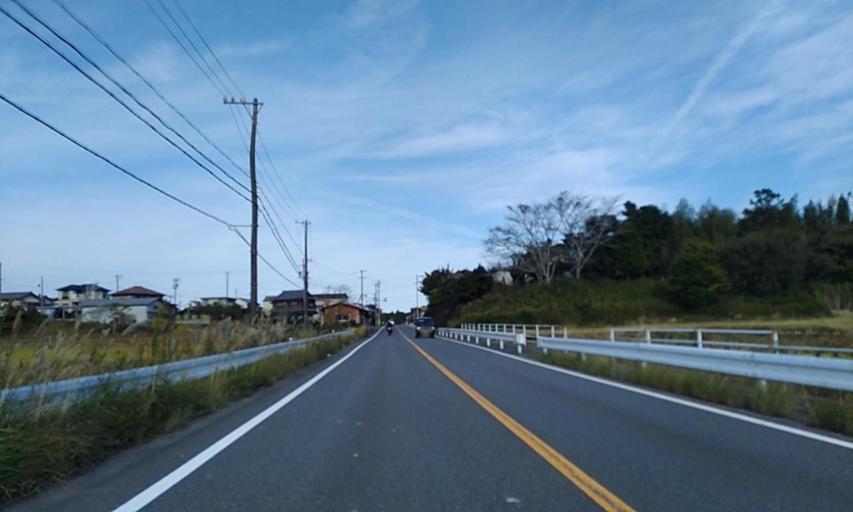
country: JP
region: Mie
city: Toba
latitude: 34.3623
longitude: 136.7764
